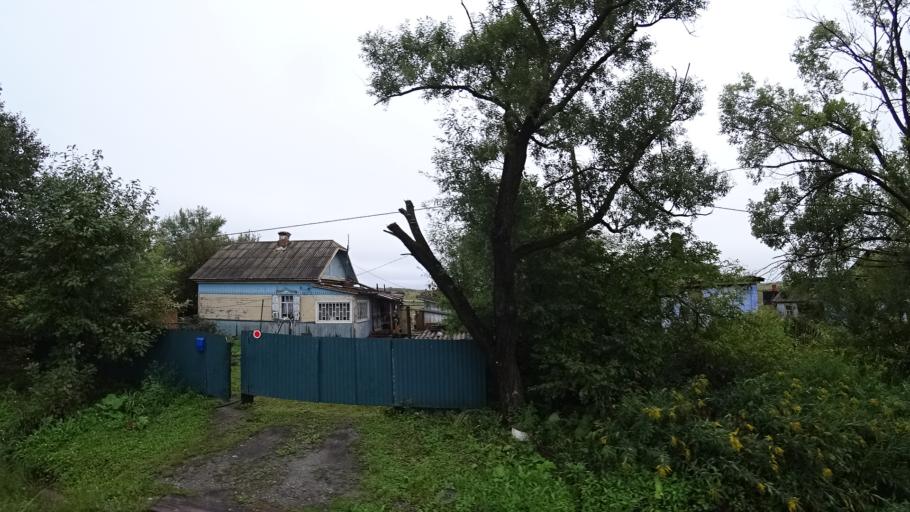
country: RU
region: Primorskiy
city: Monastyrishche
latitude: 44.1907
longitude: 132.4203
